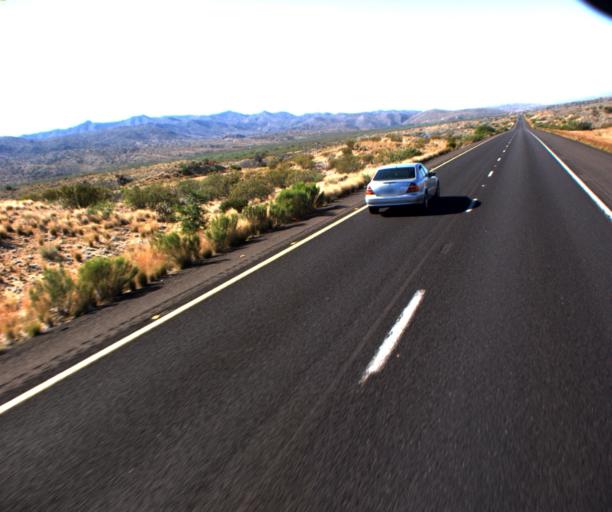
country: US
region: Arizona
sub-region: Mohave County
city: Kingman
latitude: 35.0672
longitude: -113.6658
